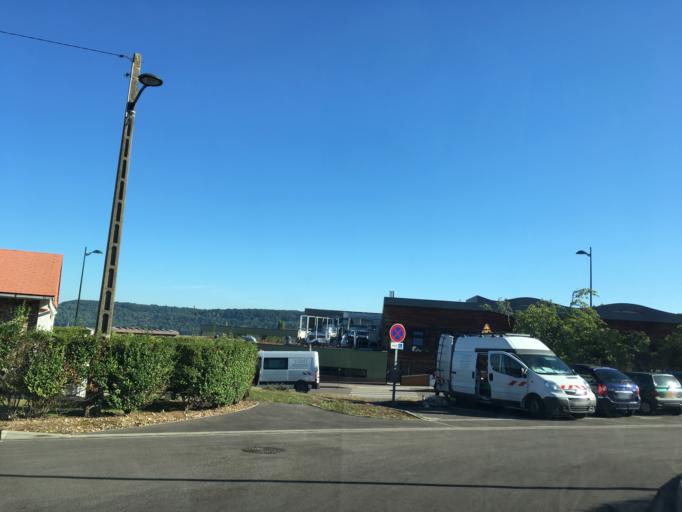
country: FR
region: Haute-Normandie
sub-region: Departement de l'Eure
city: Vernon
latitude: 49.0791
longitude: 1.4915
